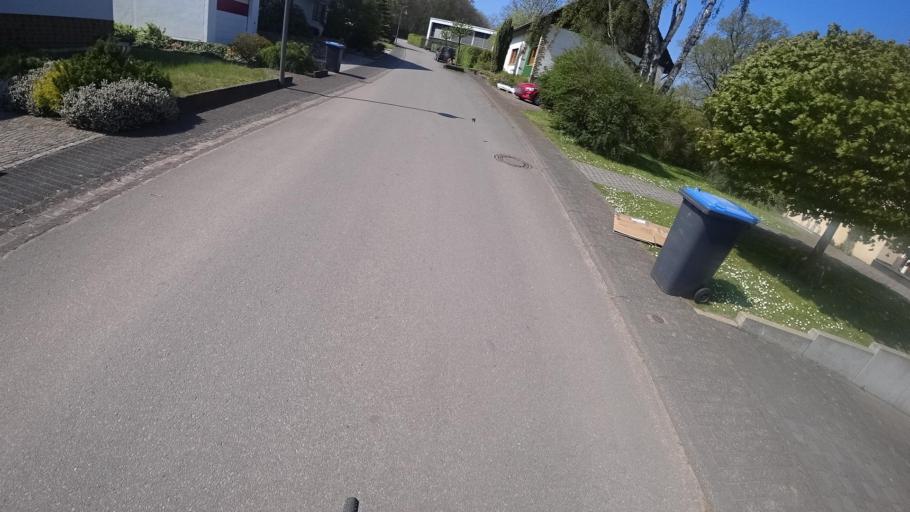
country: DE
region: Rheinland-Pfalz
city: Tawern
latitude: 49.6682
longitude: 6.5136
